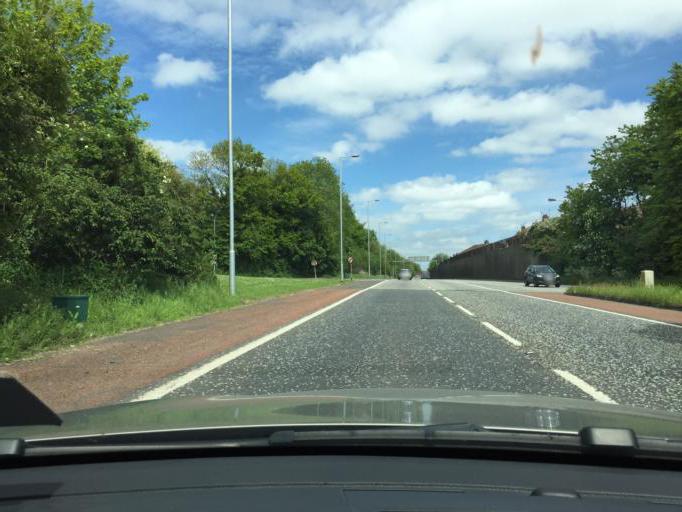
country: GB
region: Northern Ireland
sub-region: Armagh District
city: Portadown
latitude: 54.4197
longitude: -6.4560
